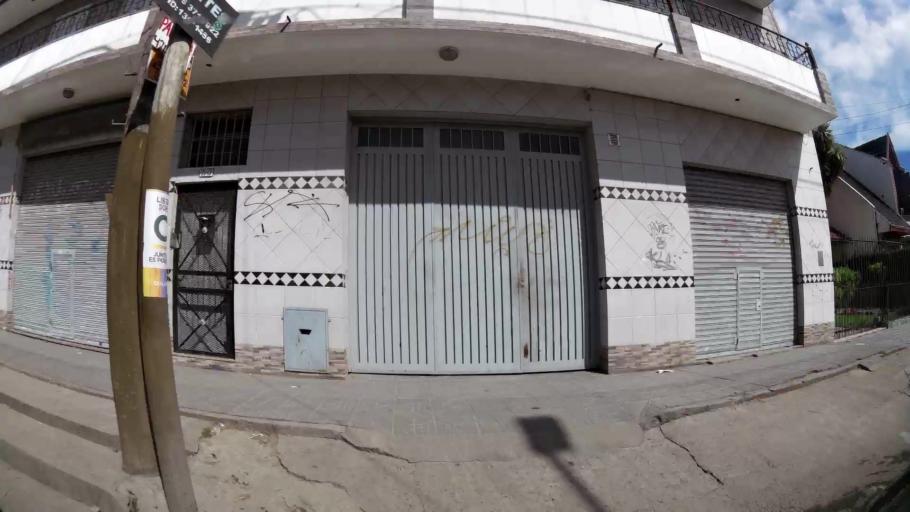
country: AR
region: Buenos Aires
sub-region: Partido de Quilmes
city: Quilmes
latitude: -34.7813
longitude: -58.3054
